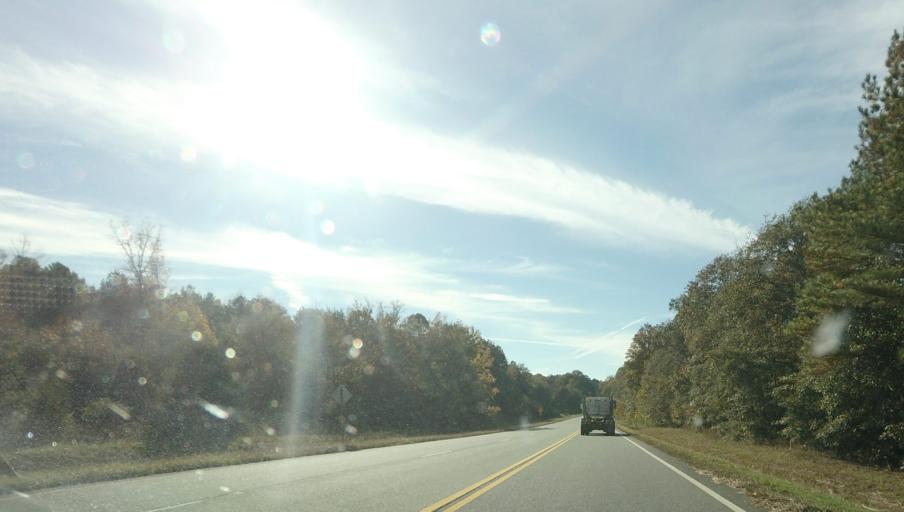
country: US
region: Georgia
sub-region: Talbot County
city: Talbotton
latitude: 32.6984
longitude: -84.4285
